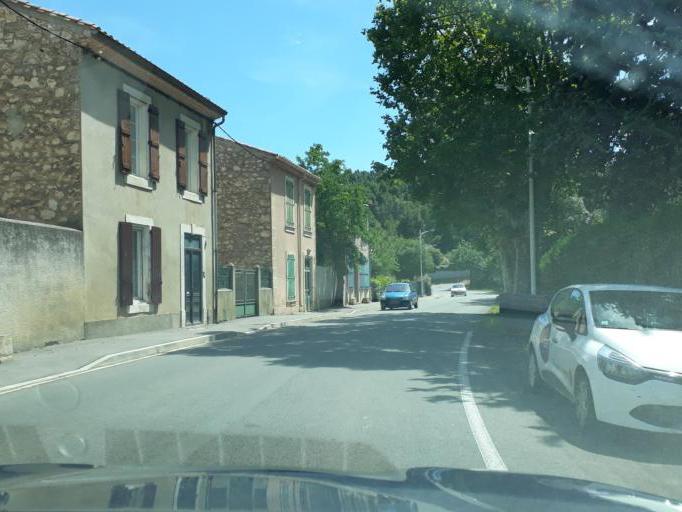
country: FR
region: Languedoc-Roussillon
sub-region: Departement de l'Aude
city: Portel-des-Corbieres
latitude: 43.0495
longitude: 2.9237
